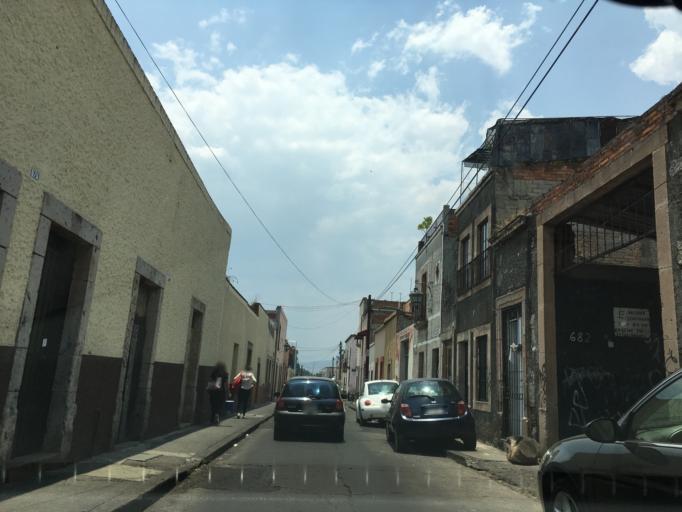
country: MX
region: Michoacan
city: Morelia
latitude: 19.6990
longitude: -101.1987
